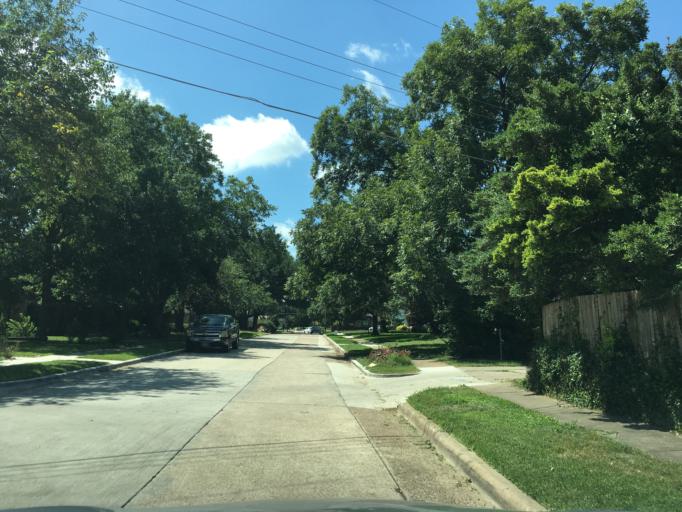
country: US
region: Texas
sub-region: Dallas County
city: Garland
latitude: 32.8489
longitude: -96.6528
